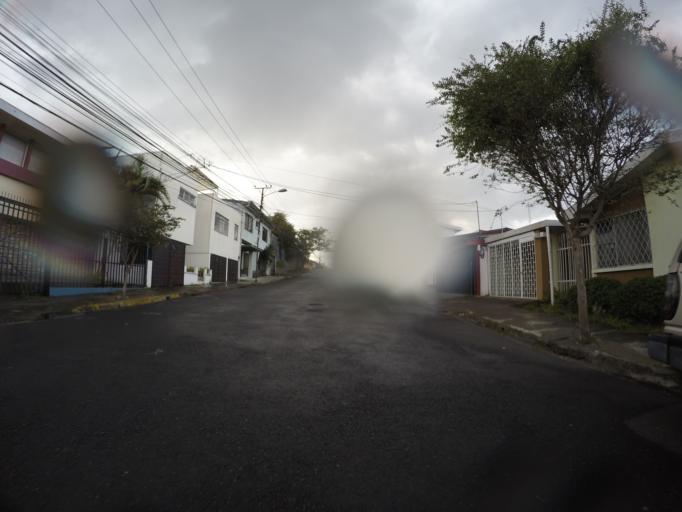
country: CR
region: San Jose
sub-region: Canton de Goicoechea
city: Guadalupe
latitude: 9.9373
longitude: -84.0624
